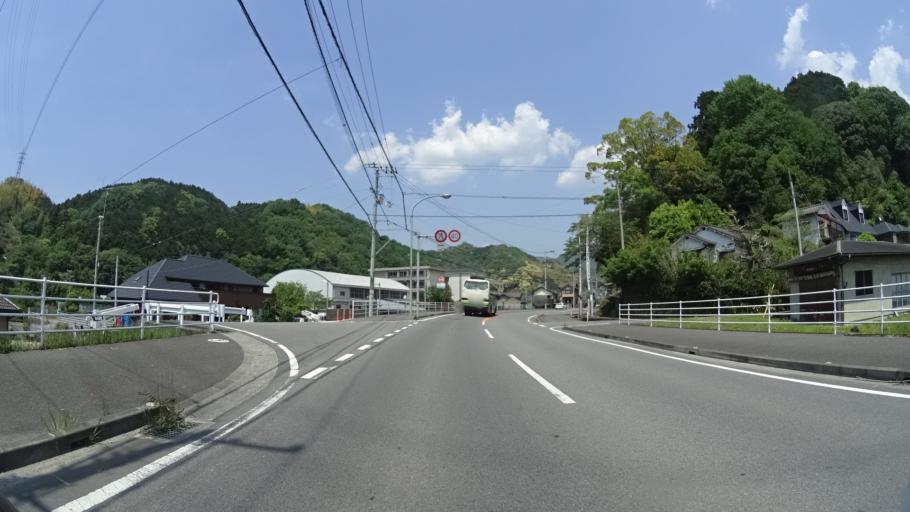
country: JP
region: Ehime
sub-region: Shikoku-chuo Shi
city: Matsuyama
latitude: 33.8590
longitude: 132.8133
